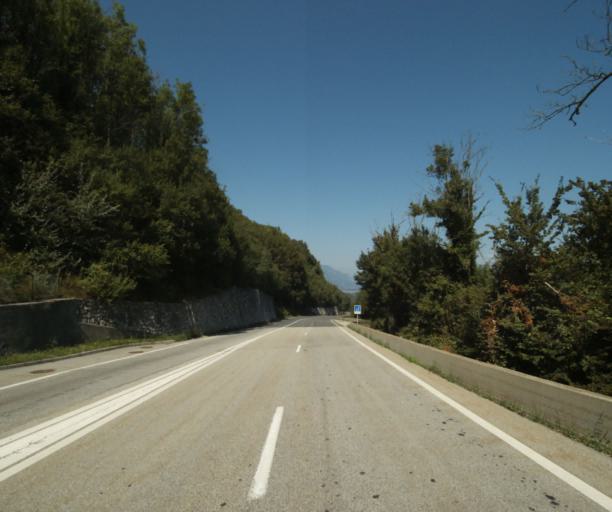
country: FR
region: Rhone-Alpes
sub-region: Departement de l'Isere
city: Notre-Dame-de-Mesage
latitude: 45.0378
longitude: 5.7669
